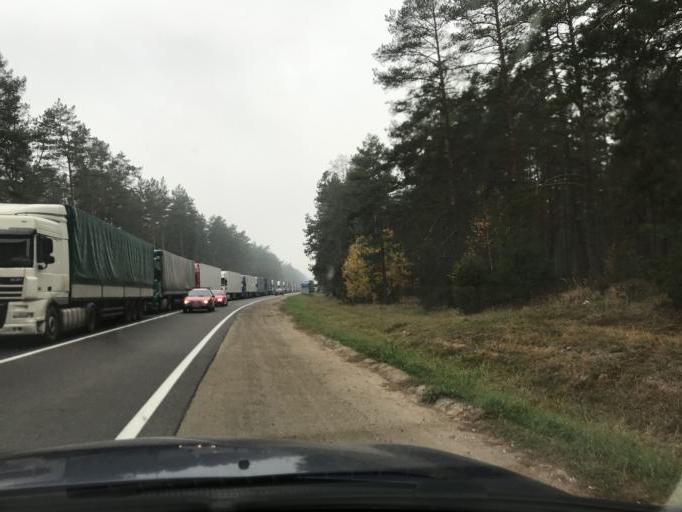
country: LT
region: Alytaus apskritis
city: Druskininkai
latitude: 53.9359
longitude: 23.9520
